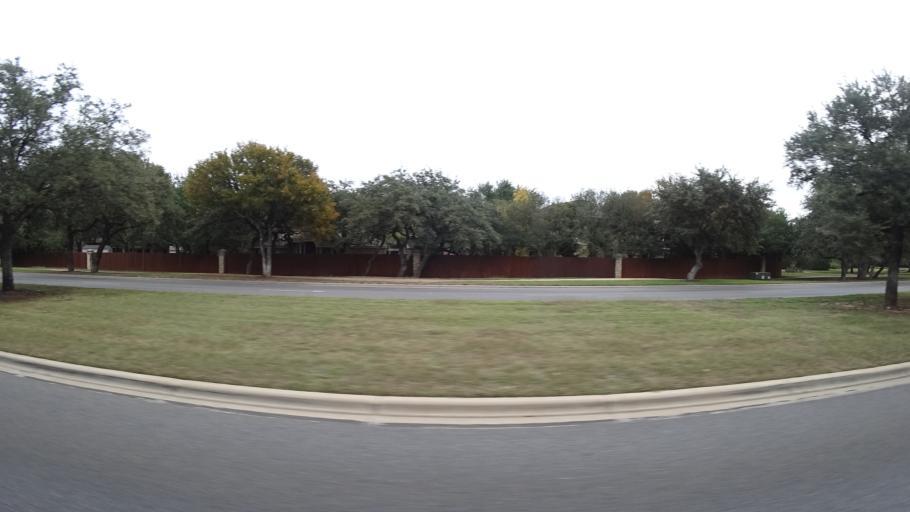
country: US
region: Texas
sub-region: Williamson County
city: Cedar Park
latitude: 30.4865
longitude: -97.8383
